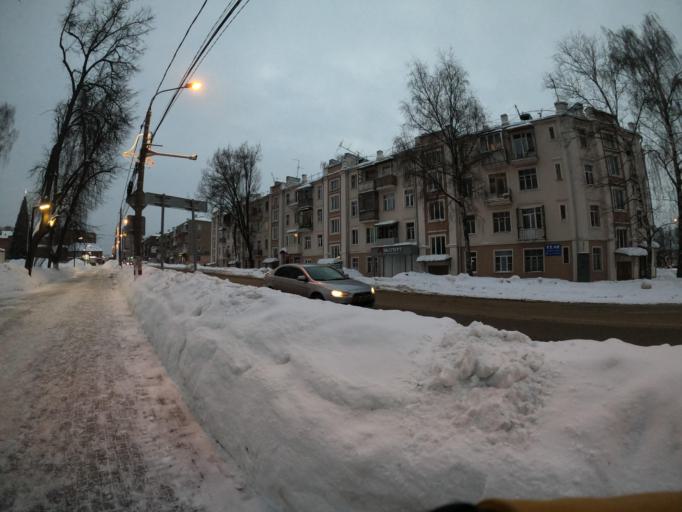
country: RU
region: Moskovskaya
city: Pavlovskiy Posad
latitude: 55.7809
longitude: 38.6710
